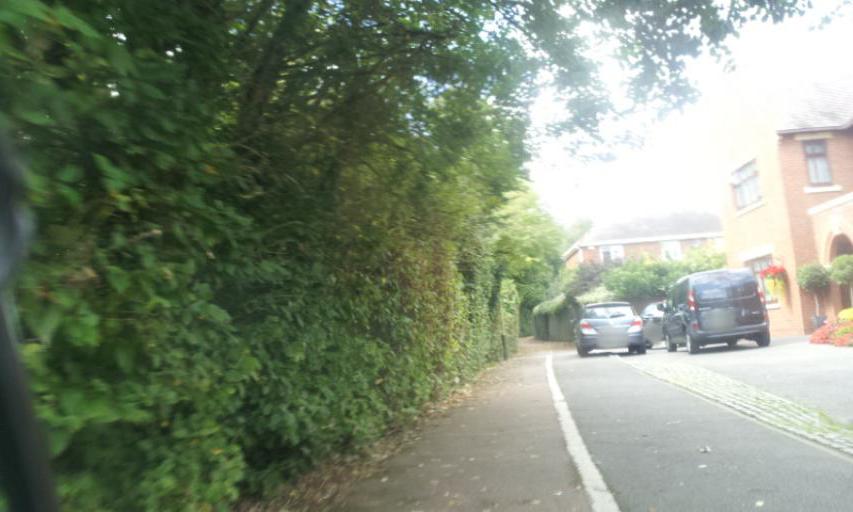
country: GB
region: England
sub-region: Kent
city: Larkfield
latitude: 51.2961
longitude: 0.4445
